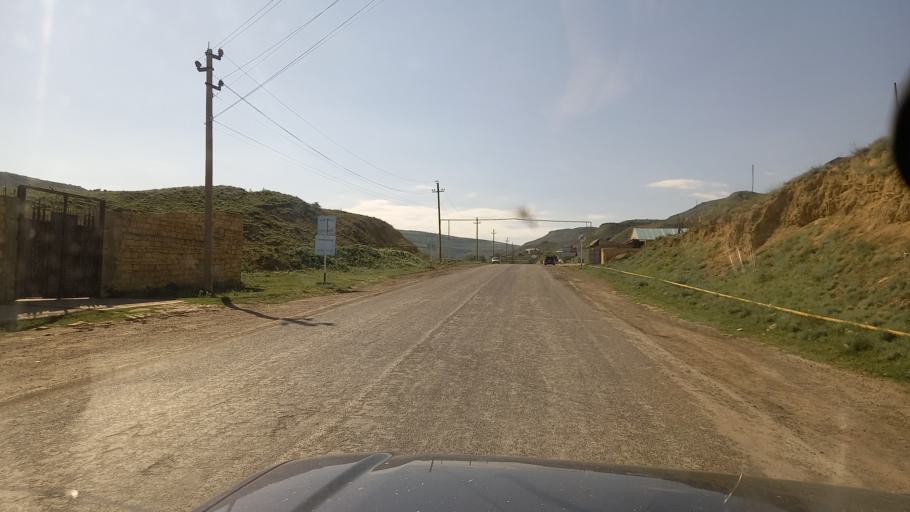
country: RU
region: Dagestan
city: Syrtych
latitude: 41.9447
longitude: 48.1655
